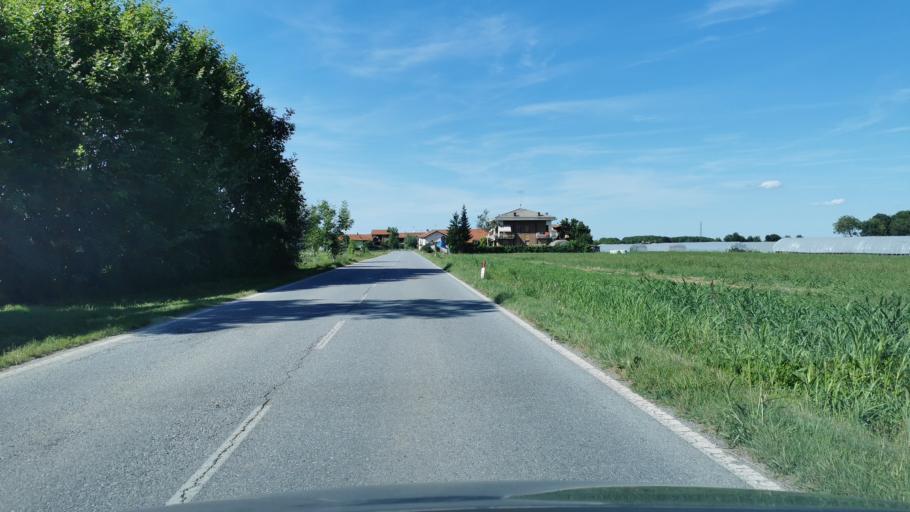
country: IT
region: Piedmont
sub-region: Provincia di Cuneo
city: Boves
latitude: 44.3447
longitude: 7.5578
